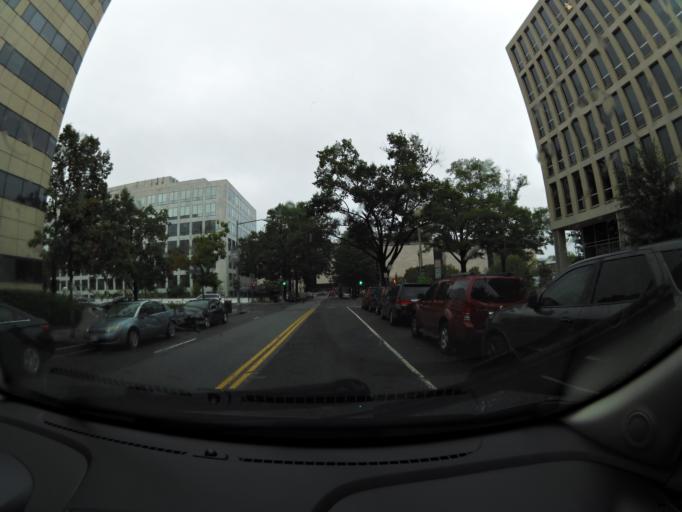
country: US
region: Washington, D.C.
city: Washington, D.C.
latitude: 38.8864
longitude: -77.0198
